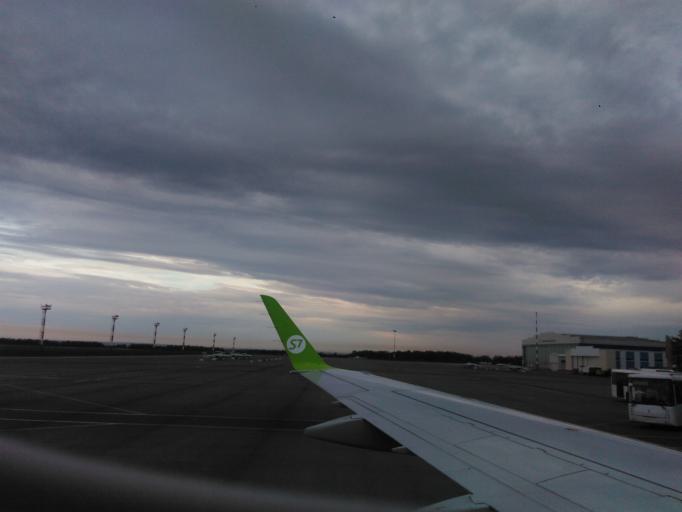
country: RU
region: Tatarstan
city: Yelabuga
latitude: 55.5659
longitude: 52.0978
